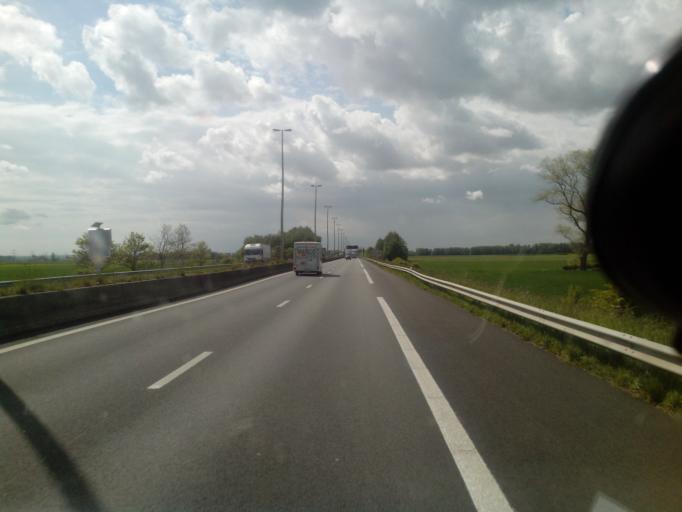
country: FR
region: Nord-Pas-de-Calais
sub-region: Departement du Pas-de-Calais
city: Marck
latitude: 50.9342
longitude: 1.9910
